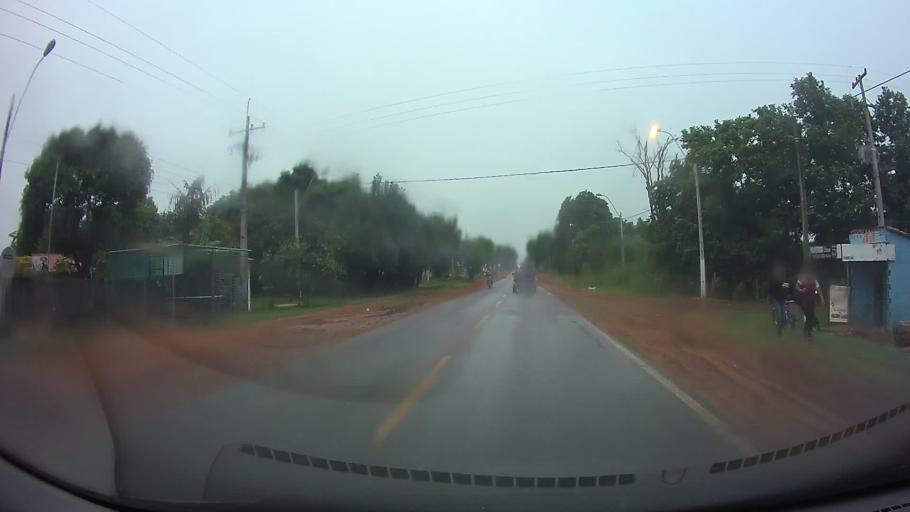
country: PY
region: Central
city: Ita
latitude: -25.4657
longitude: -57.3653
